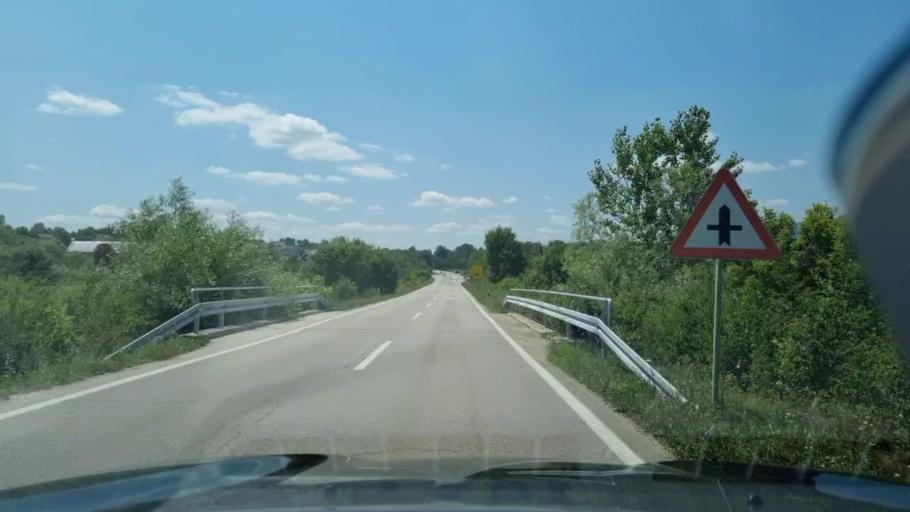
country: BA
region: Federation of Bosnia and Herzegovina
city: Peci
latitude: 44.6880
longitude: 16.7359
